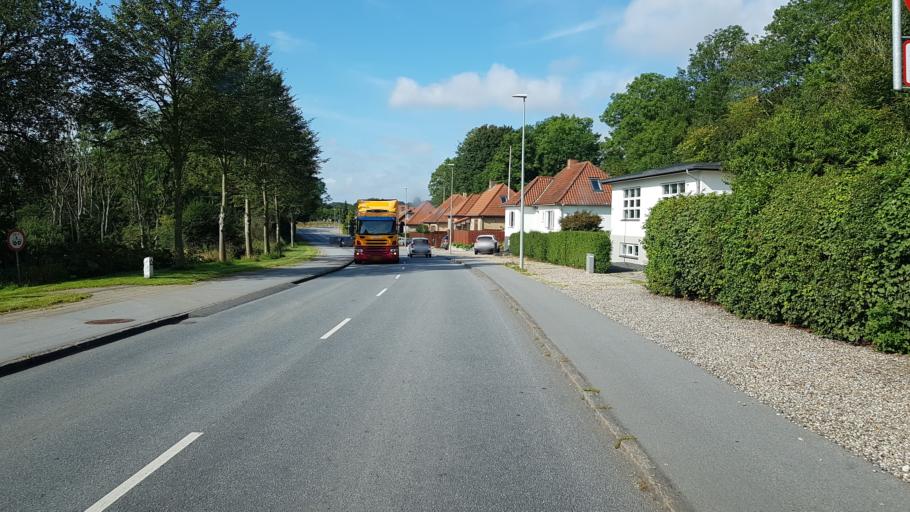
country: DK
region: South Denmark
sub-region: Haderslev Kommune
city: Haderslev
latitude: 55.2481
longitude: 9.4594
